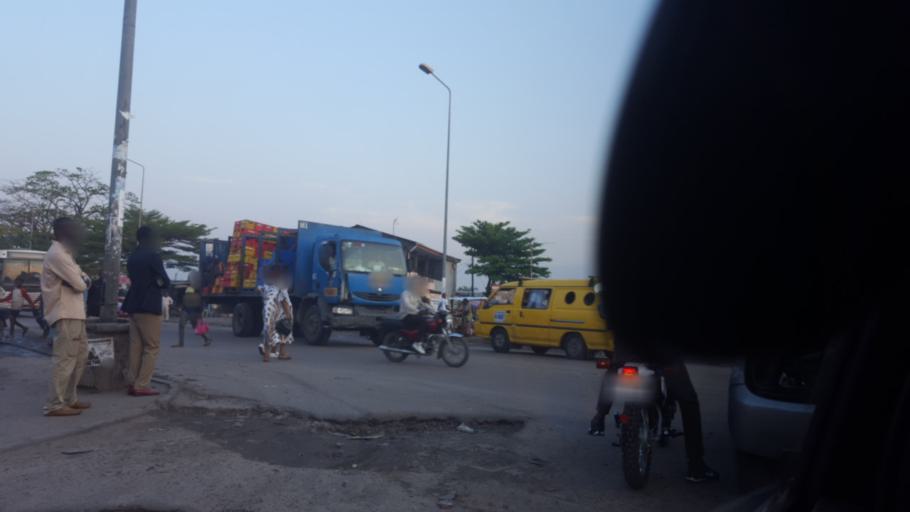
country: CD
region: Kinshasa
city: Kinshasa
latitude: -4.3426
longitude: 15.3196
